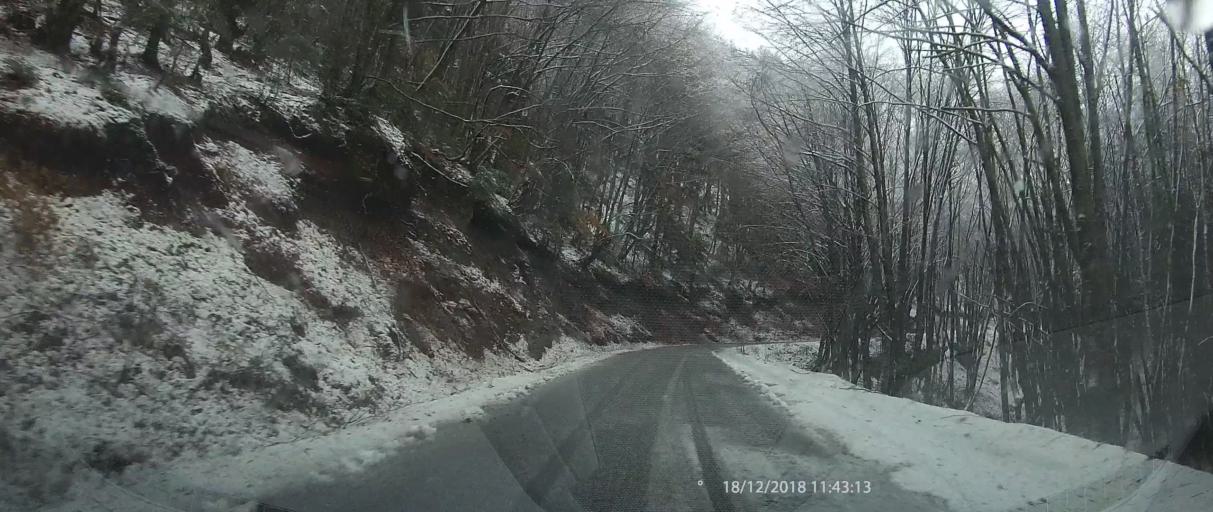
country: GR
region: Central Macedonia
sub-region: Nomos Pierias
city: Litochoro
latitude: 40.1093
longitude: 22.4690
